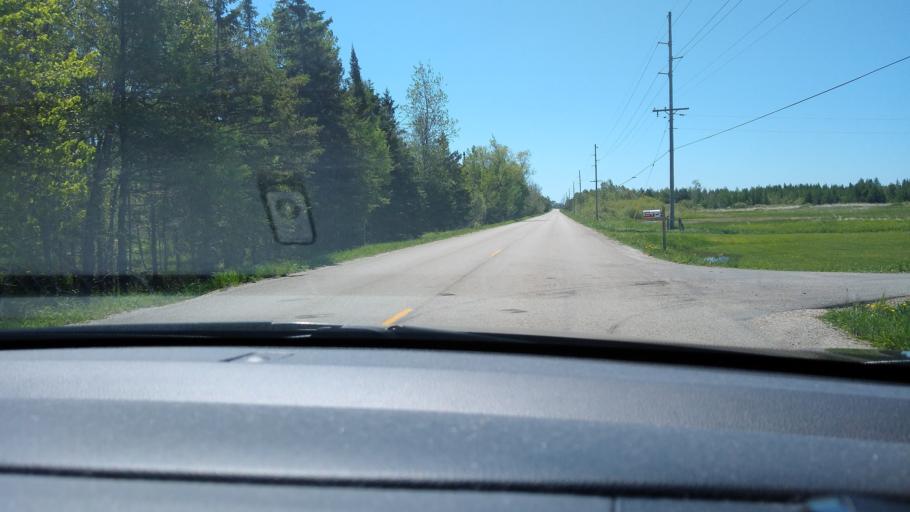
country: US
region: Michigan
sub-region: Delta County
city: Gladstone
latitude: 45.8585
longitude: -87.1841
